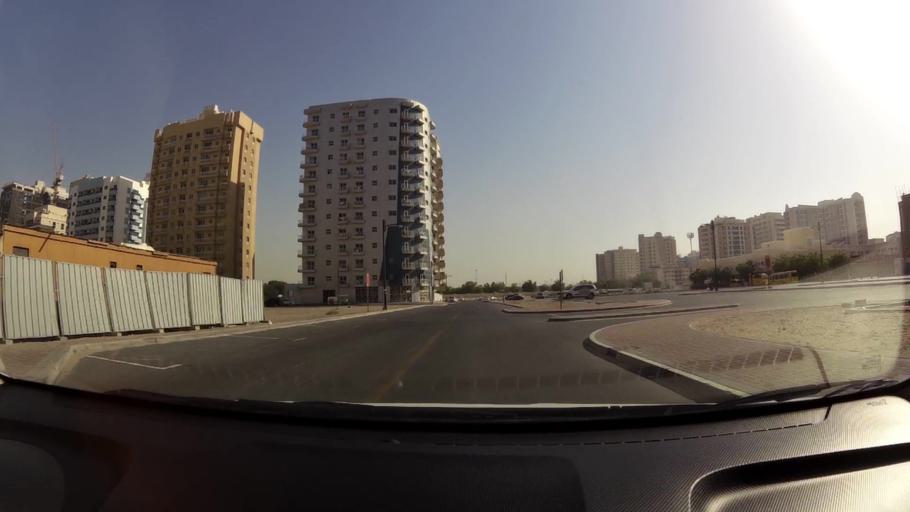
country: AE
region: Ash Shariqah
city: Sharjah
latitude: 25.2906
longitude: 55.3763
